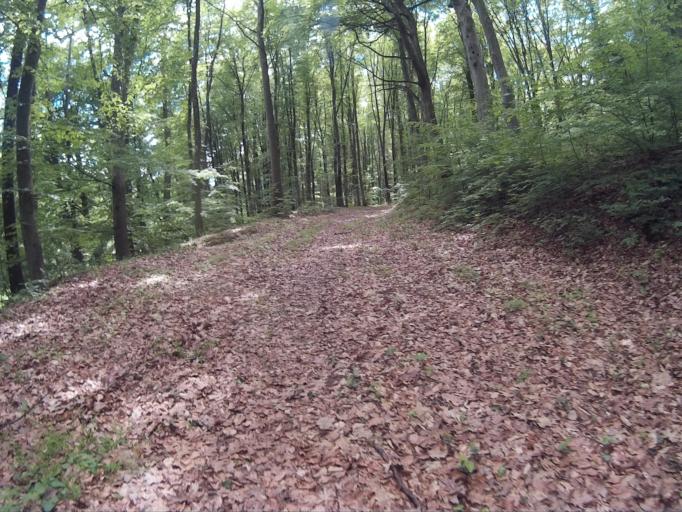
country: HU
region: Vas
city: Kormend
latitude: 46.9597
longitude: 16.5408
